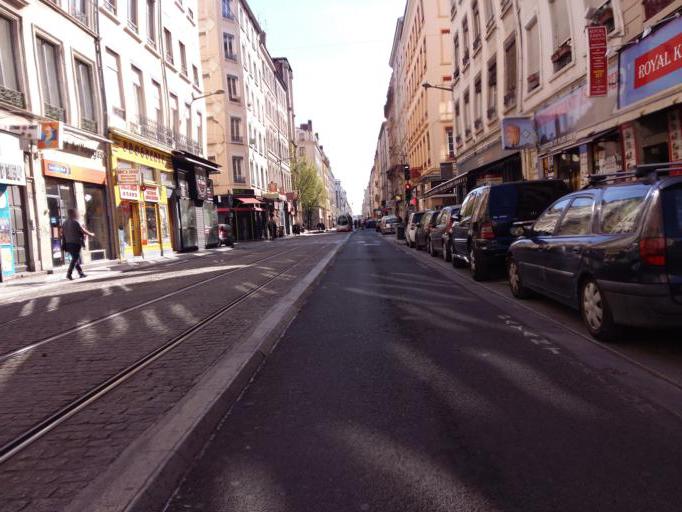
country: FR
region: Rhone-Alpes
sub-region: Departement du Rhone
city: Lyon
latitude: 45.7540
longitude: 4.8417
